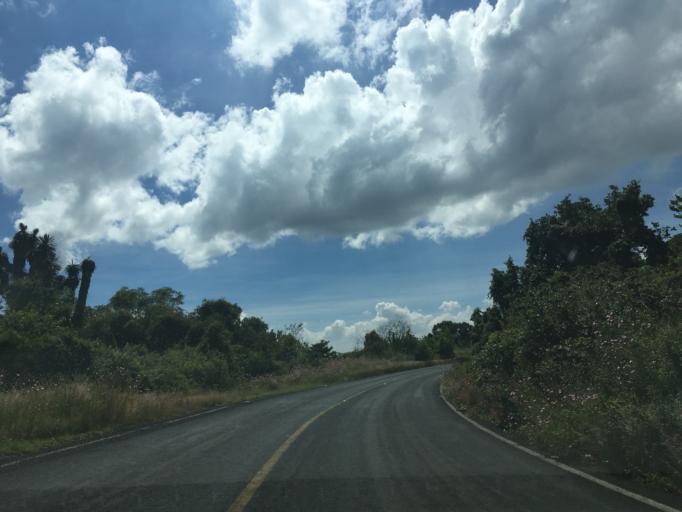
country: MX
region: Michoacan
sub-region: Morelia
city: Cuto de la Esperanza
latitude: 19.7396
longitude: -101.3507
